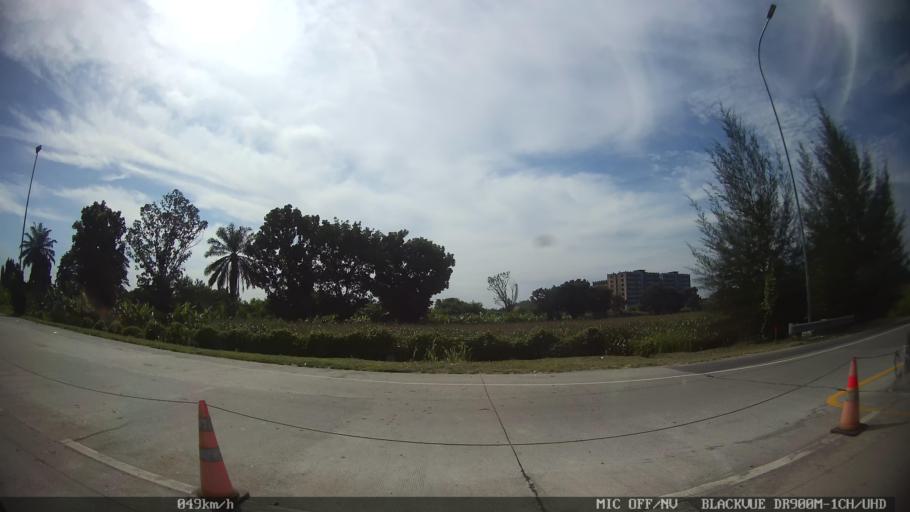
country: ID
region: North Sumatra
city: Sunggal
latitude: 3.6287
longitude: 98.6312
